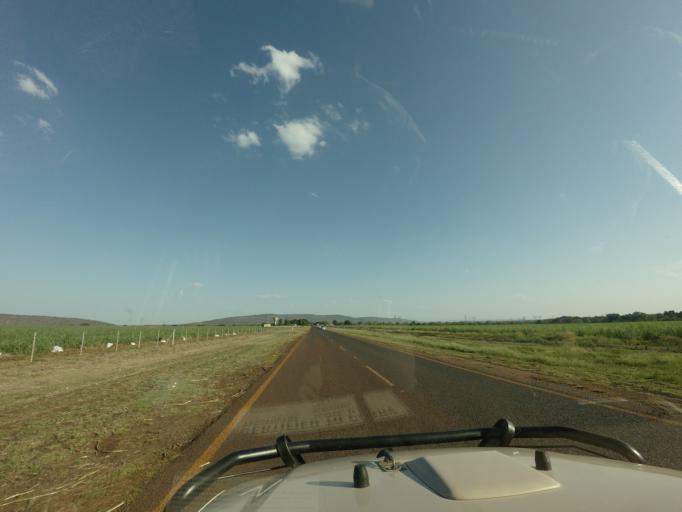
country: ZA
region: Mpumalanga
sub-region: Ehlanzeni District
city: Komatipoort
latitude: -25.4222
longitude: 31.9430
